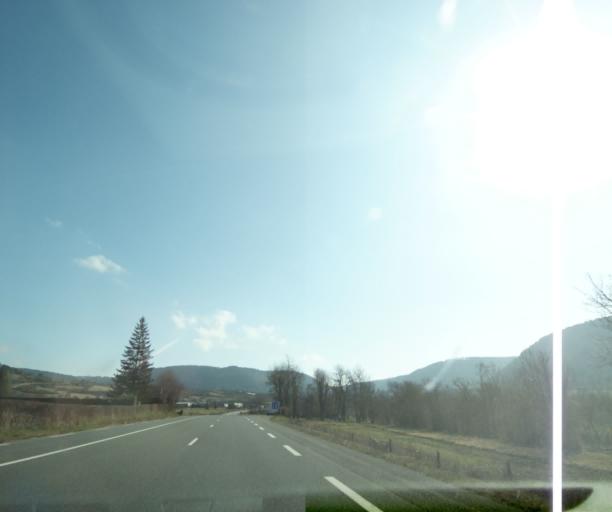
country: FR
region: Languedoc-Roussillon
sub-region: Departement de la Lozere
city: Chanac
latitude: 44.4789
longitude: 3.3257
